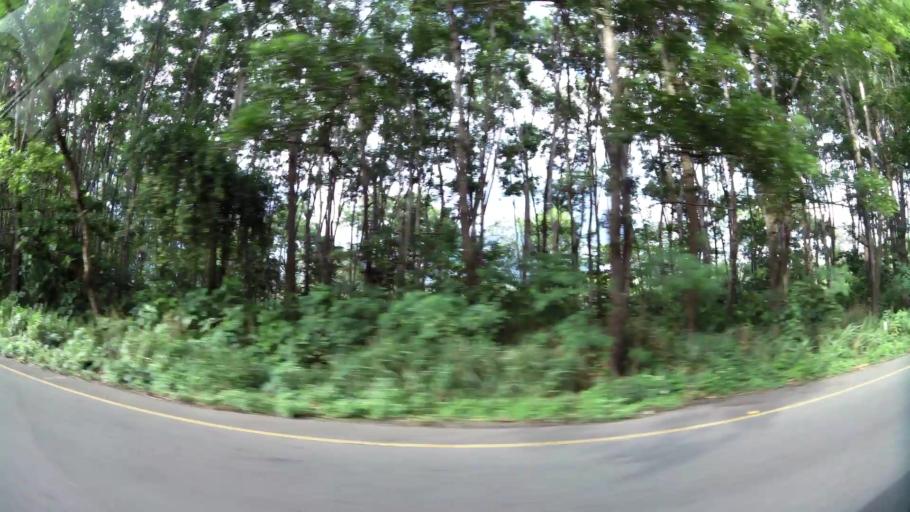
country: DO
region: Monsenor Nouel
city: Piedra Blanca
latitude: 18.8603
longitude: -70.3488
